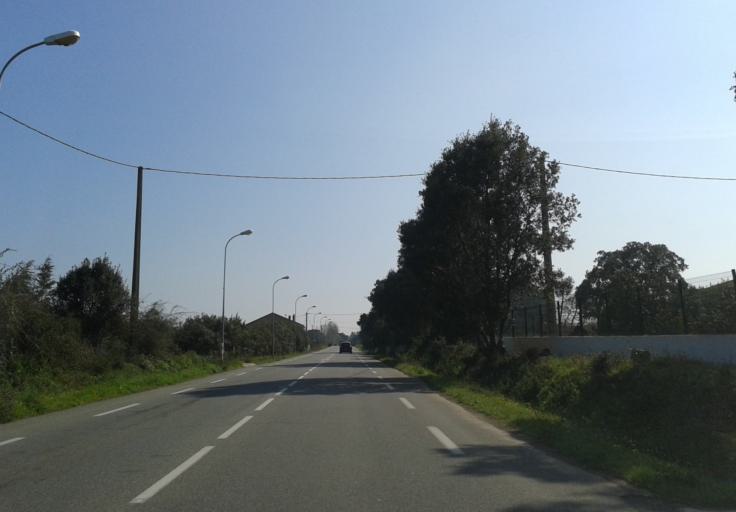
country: FR
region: Corsica
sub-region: Departement de la Haute-Corse
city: Cervione
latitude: 42.3146
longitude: 9.5413
